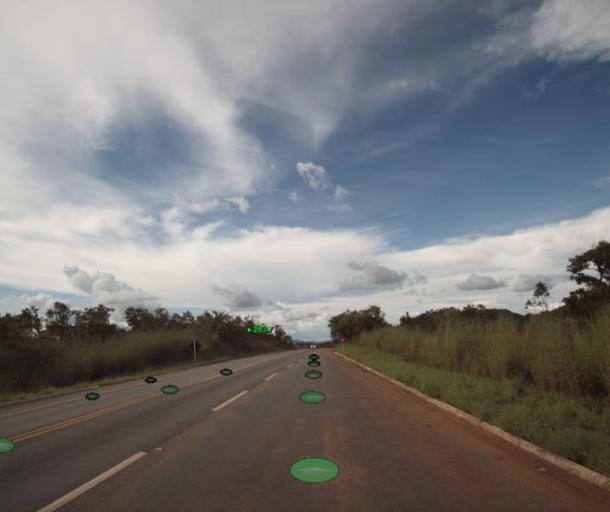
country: BR
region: Goias
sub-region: Barro Alto
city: Barro Alto
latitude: -15.1003
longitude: -48.7484
